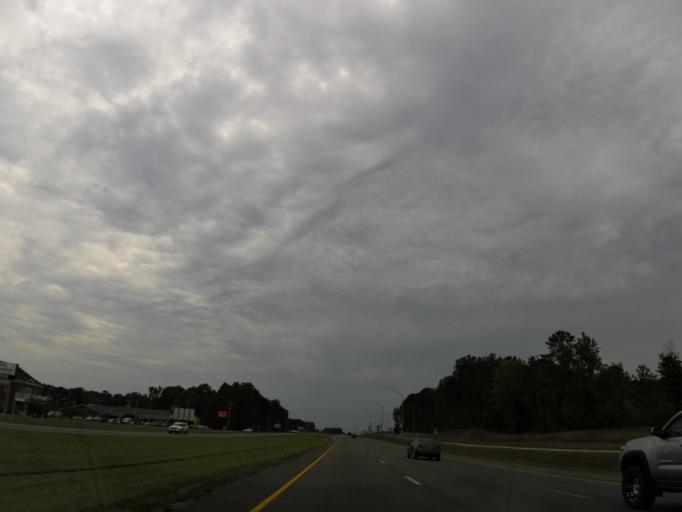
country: US
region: Alabama
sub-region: Jackson County
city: Scottsboro
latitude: 34.6613
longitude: -86.0171
